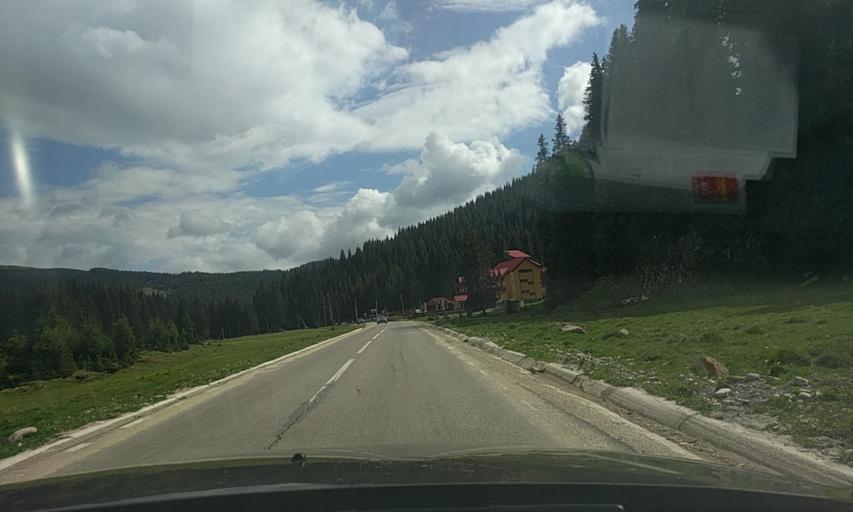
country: RO
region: Prahova
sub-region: Oras Busteni
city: Busteni
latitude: 45.3784
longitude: 25.4351
